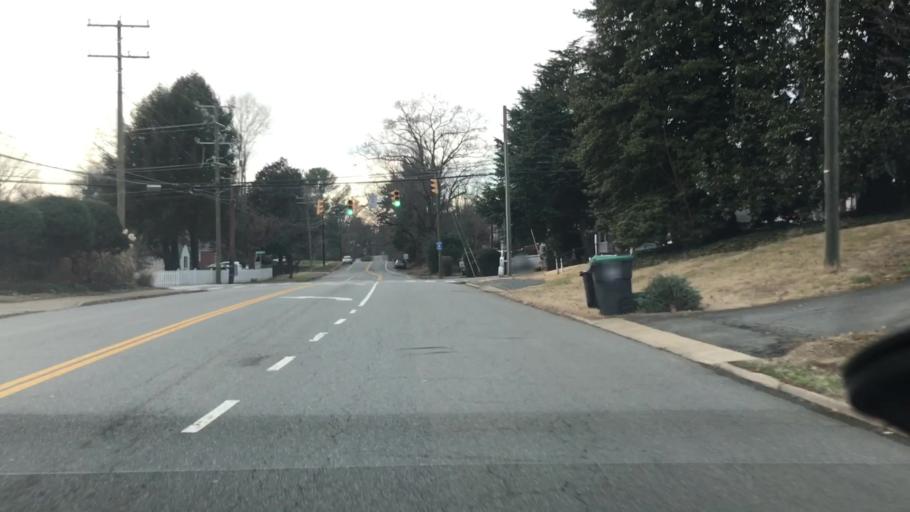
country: US
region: Virginia
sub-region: City of Charlottesville
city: Charlottesville
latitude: 38.0453
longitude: -78.4831
